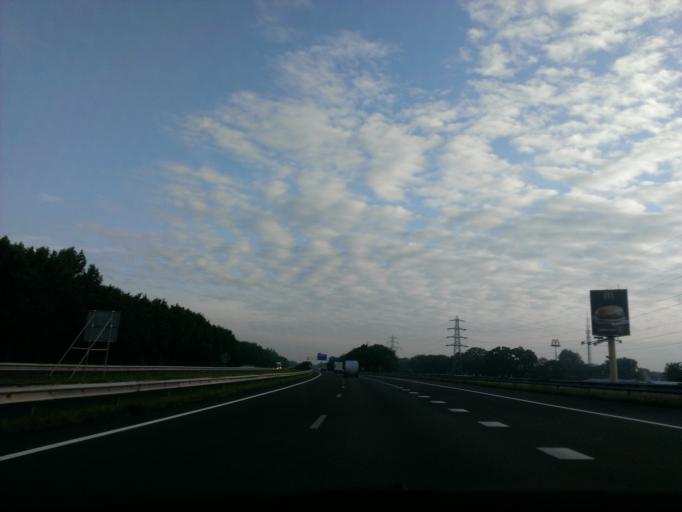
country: NL
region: Drenthe
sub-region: Gemeente Hoogeveen
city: Hoogeveen
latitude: 52.7170
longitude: 6.4648
